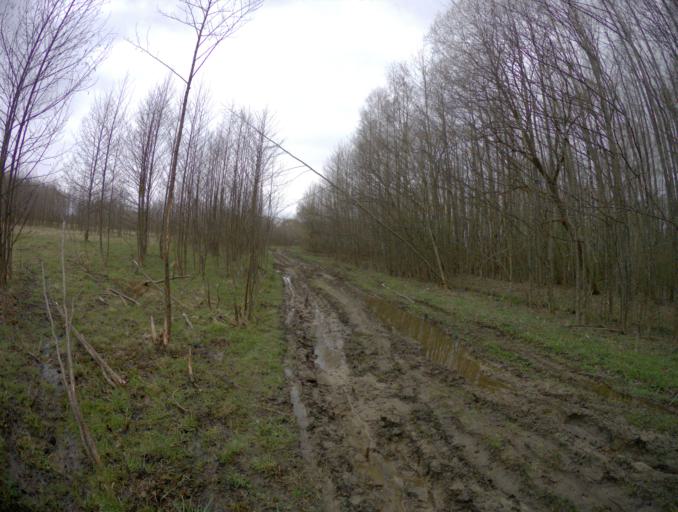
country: RU
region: Vladimir
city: Sudogda
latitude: 56.0149
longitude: 40.8051
